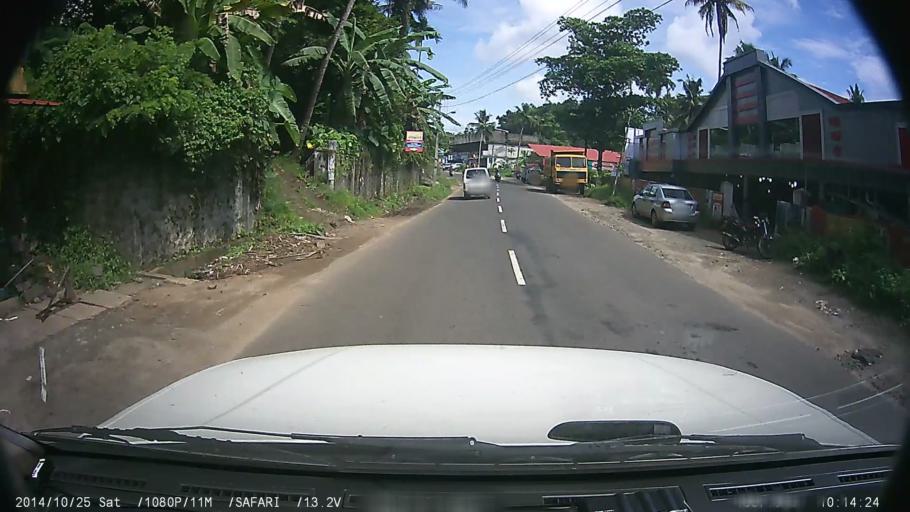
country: IN
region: Kerala
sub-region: Ernakulam
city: Piravam
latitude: 9.8675
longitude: 76.5968
